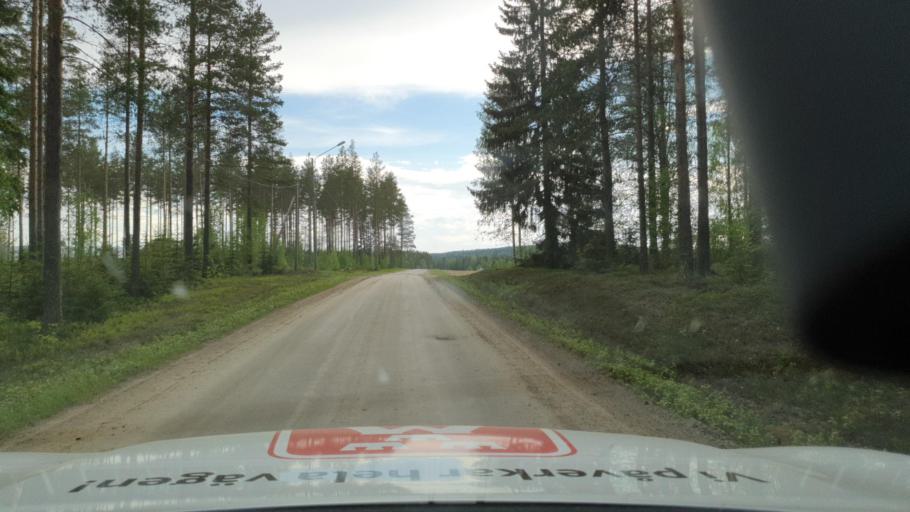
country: SE
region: Vaesterbotten
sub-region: Vannas Kommun
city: Vannasby
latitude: 64.1046
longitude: 19.9467
